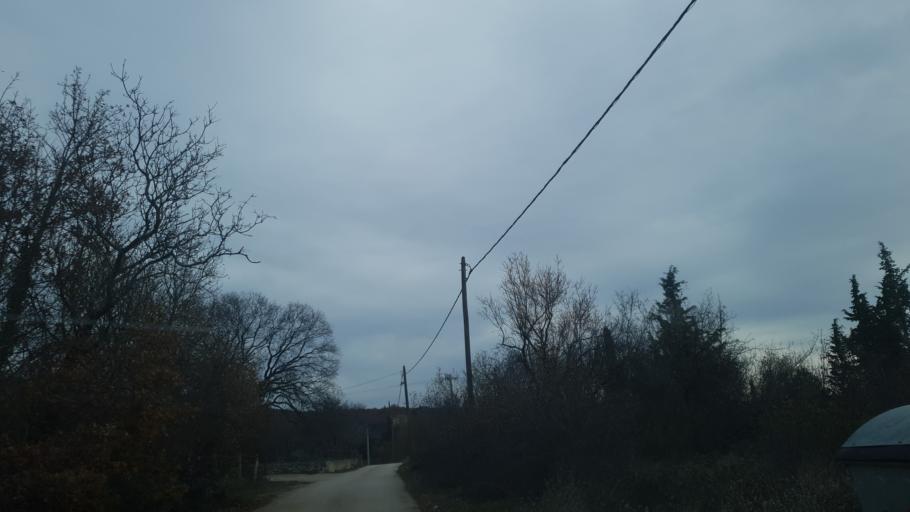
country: HR
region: Splitsko-Dalmatinska
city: Imotski
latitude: 43.4454
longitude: 17.2419
